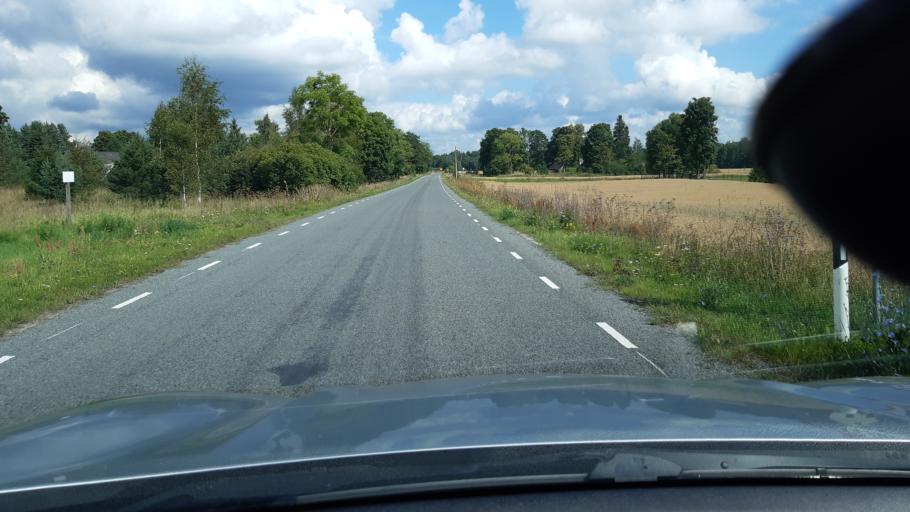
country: EE
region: Raplamaa
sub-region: Kehtna vald
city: Kehtna
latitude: 58.8747
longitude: 25.0077
